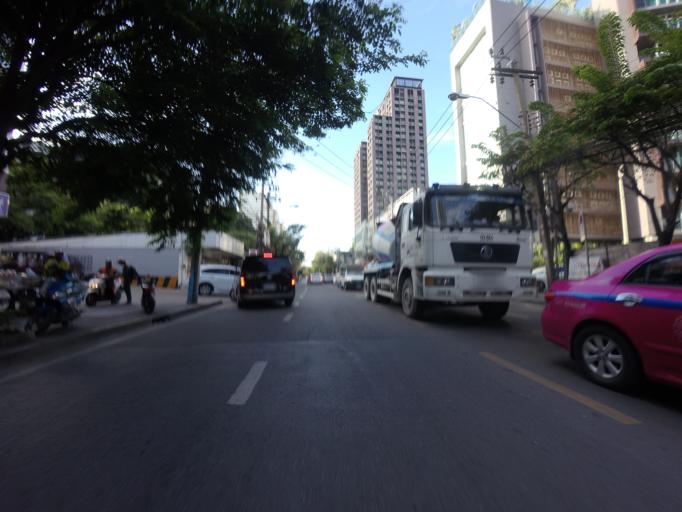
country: TH
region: Bangkok
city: Watthana
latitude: 13.7205
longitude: 100.5845
